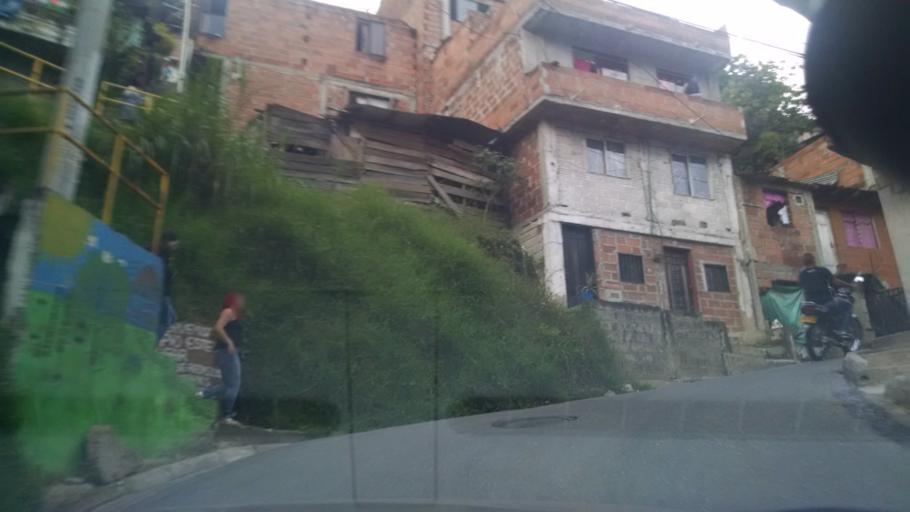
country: CO
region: Antioquia
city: Medellin
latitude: 6.2681
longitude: -75.6139
